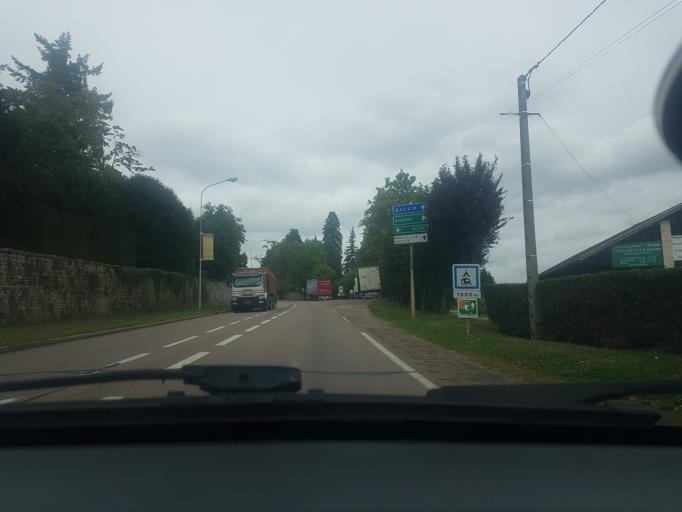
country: FR
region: Bourgogne
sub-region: Departement de la Cote-d'Or
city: Arnay-le-Duc
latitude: 47.1288
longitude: 4.4910
